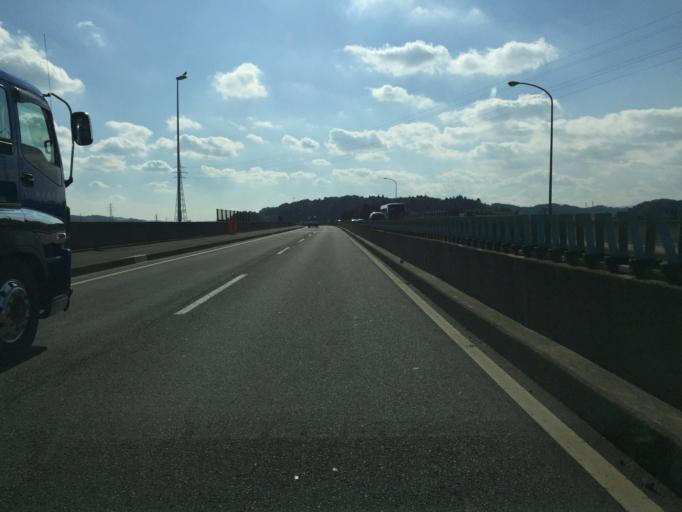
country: JP
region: Fukushima
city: Nihommatsu
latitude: 37.6055
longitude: 140.4663
